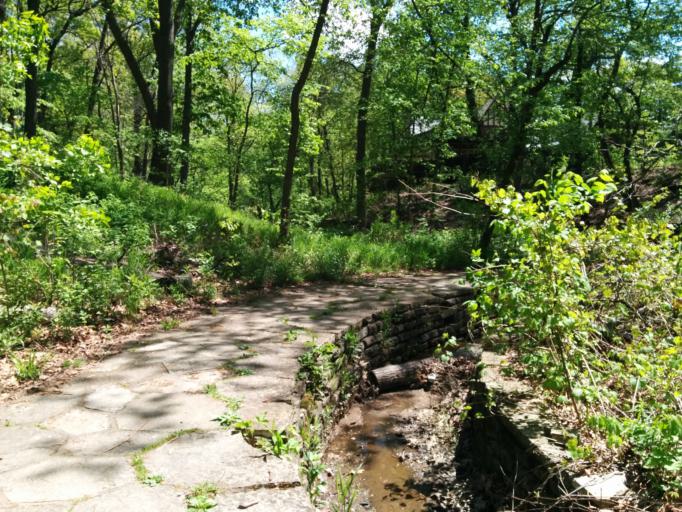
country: US
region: Illinois
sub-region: Cook County
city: Evergreen Park
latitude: 41.7339
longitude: -87.6776
